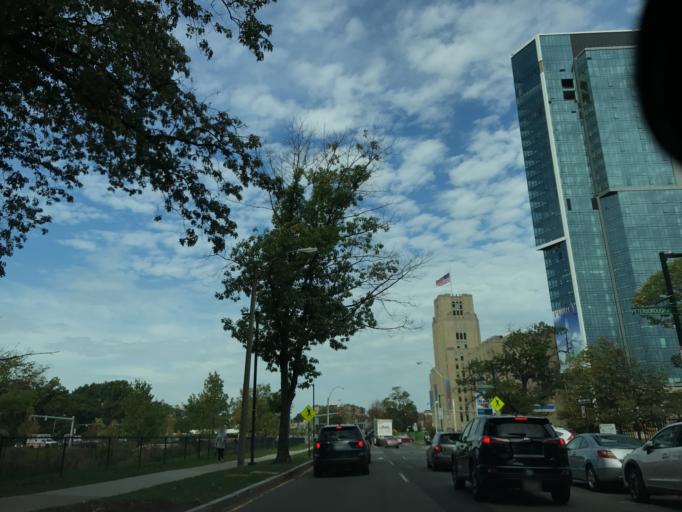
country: US
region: Massachusetts
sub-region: Norfolk County
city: Brookline
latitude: 42.3423
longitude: -71.1016
